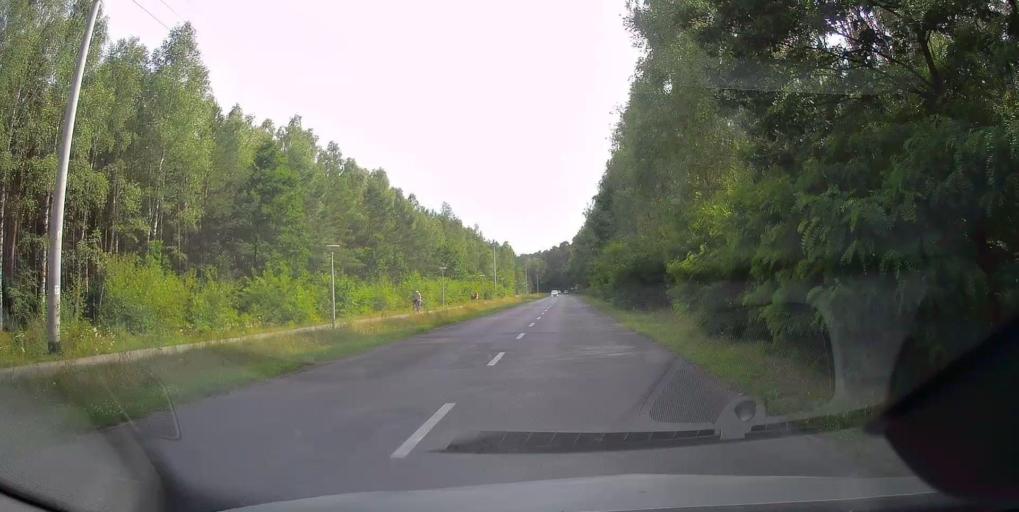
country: PL
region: Lodz Voivodeship
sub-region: Powiat tomaszowski
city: Tomaszow Mazowiecki
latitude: 51.5048
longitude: 19.9966
